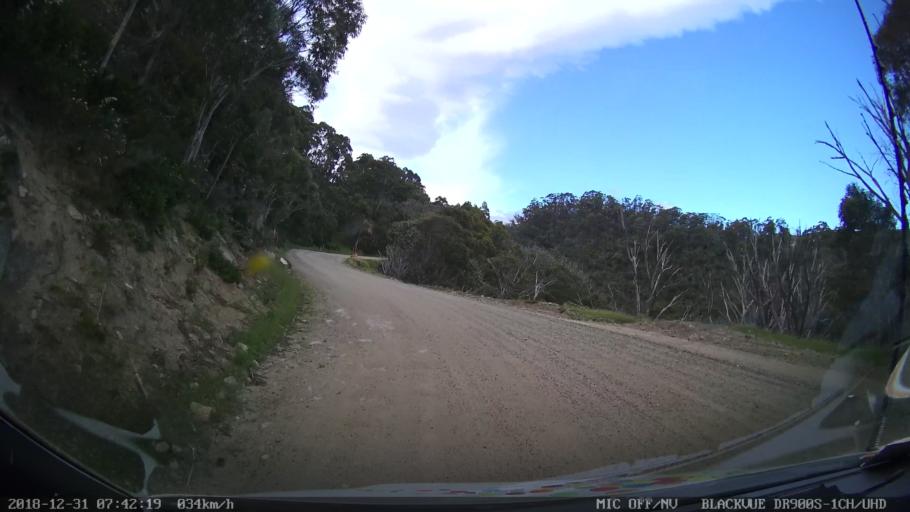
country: AU
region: New South Wales
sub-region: Snowy River
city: Jindabyne
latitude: -36.3564
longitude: 148.4100
